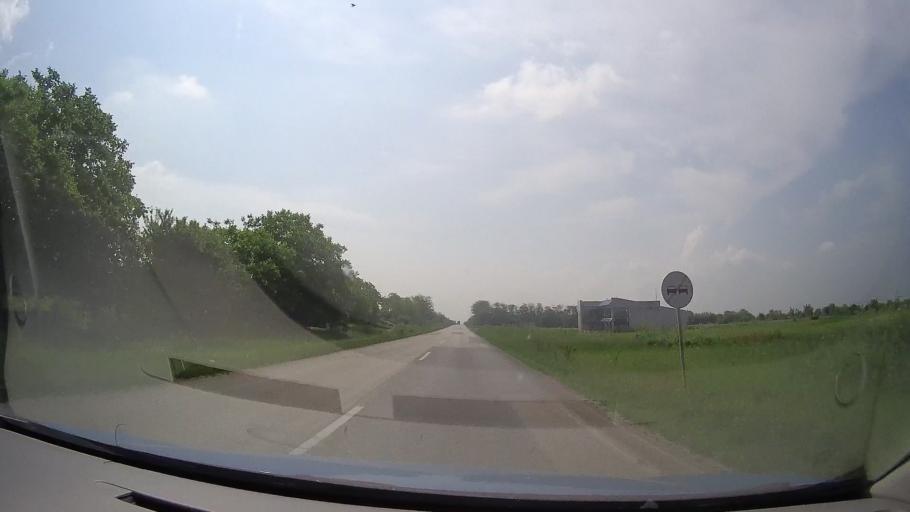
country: RS
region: Autonomna Pokrajina Vojvodina
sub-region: Juznobanatski Okrug
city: Kovacica
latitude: 45.0990
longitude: 20.6265
